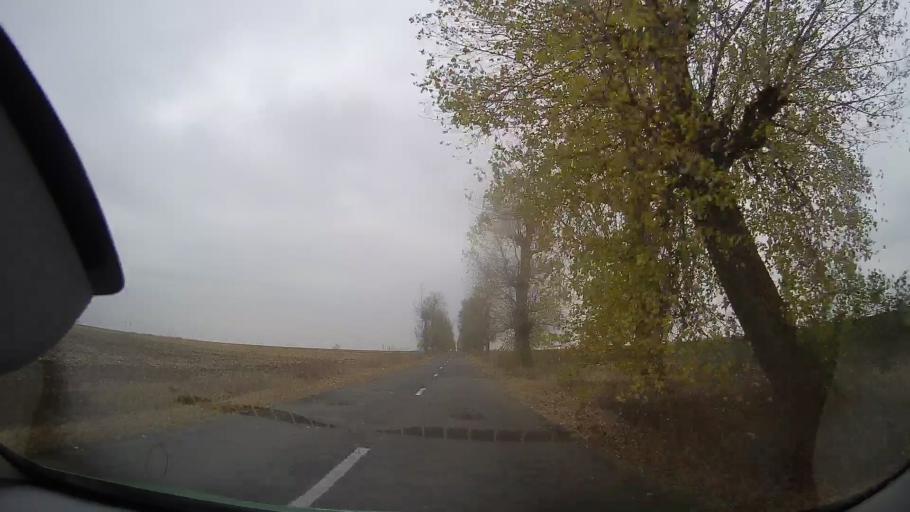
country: RO
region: Ialomita
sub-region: Comuna Grindu
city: Grindu
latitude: 44.7690
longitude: 26.8835
